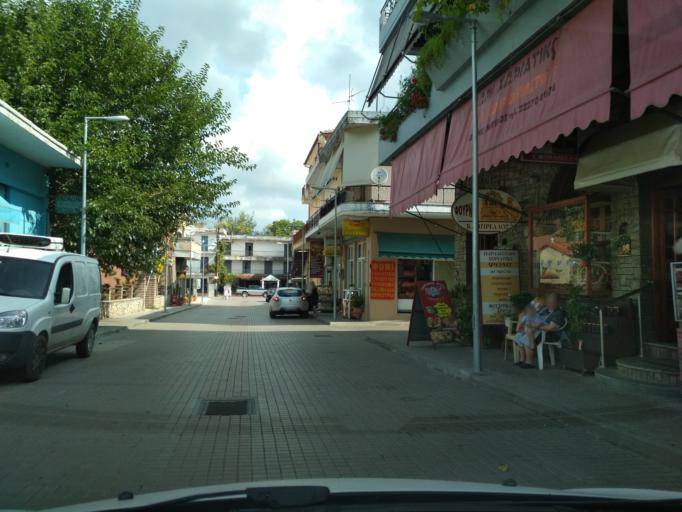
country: GR
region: Central Greece
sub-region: Nomos Evvoias
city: Prokopion
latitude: 38.7342
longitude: 23.4925
